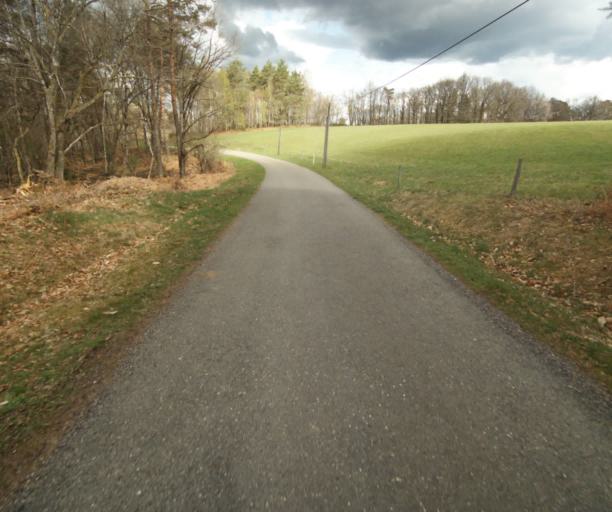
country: FR
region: Limousin
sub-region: Departement de la Correze
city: Correze
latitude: 45.2486
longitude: 1.9101
